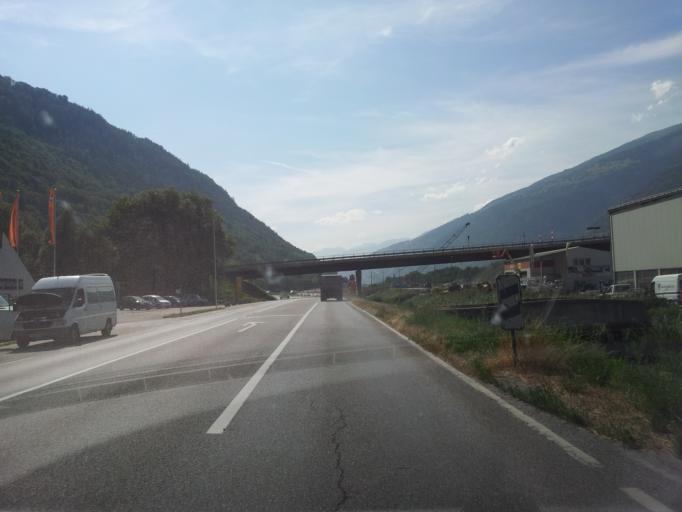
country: CH
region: Valais
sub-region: Raron District
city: Raron
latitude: 46.3043
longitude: 7.7932
